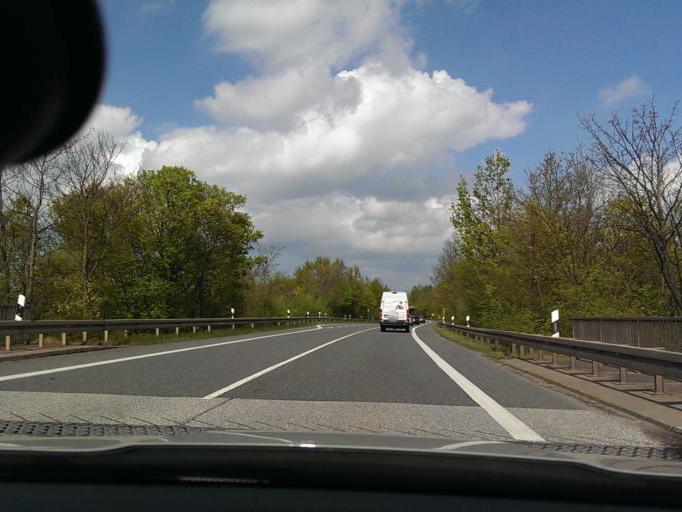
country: DE
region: Lower Saxony
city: Laatzen
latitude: 52.2910
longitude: 9.8169
